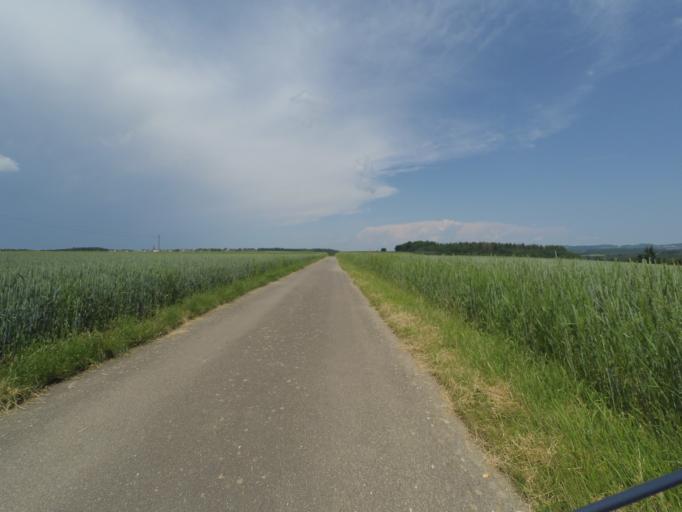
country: DE
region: Rheinland-Pfalz
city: Beulich
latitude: 50.1811
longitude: 7.4559
